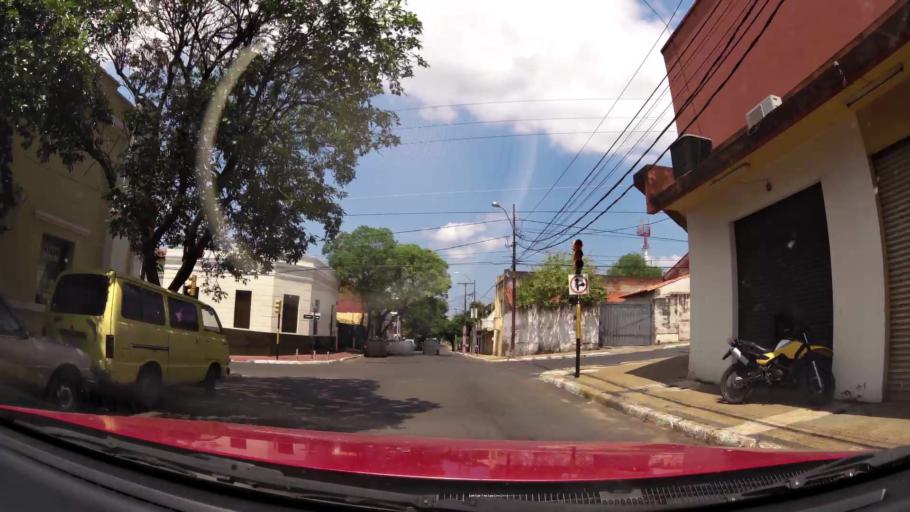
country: PY
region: Asuncion
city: Asuncion
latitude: -25.2928
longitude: -57.6334
